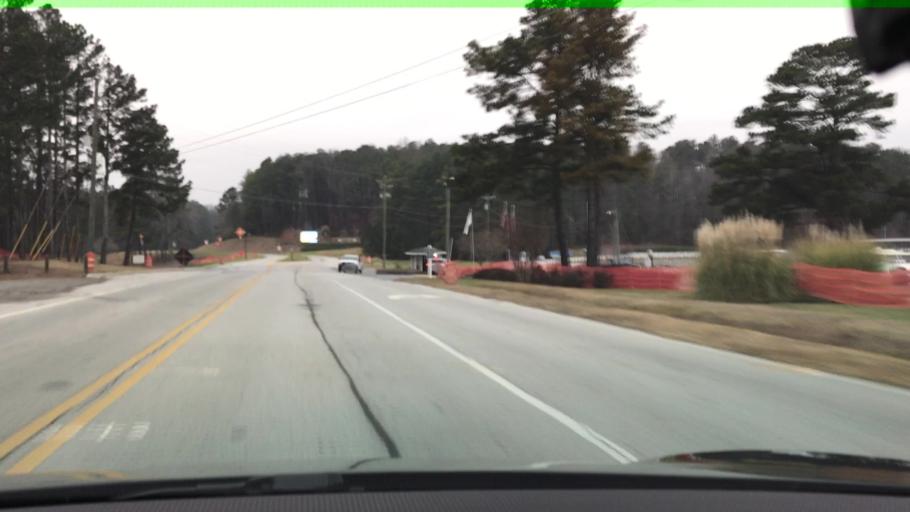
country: US
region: Georgia
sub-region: Gwinnett County
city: Buford
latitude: 34.1687
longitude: -84.0043
